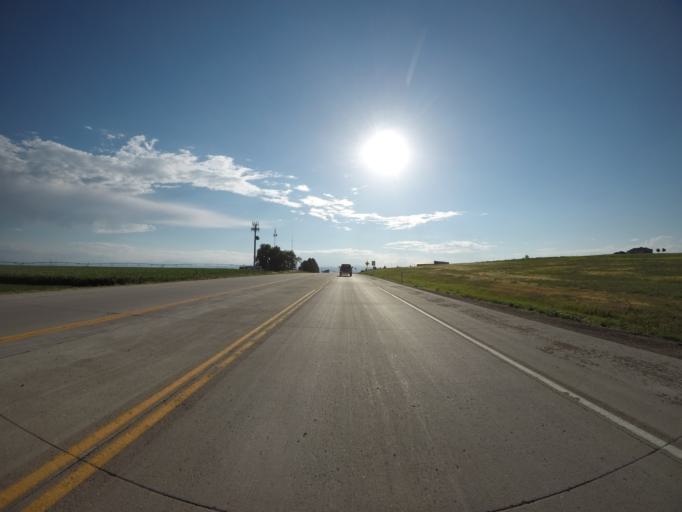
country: US
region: Colorado
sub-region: Weld County
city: Severance
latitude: 40.5816
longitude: -104.9025
